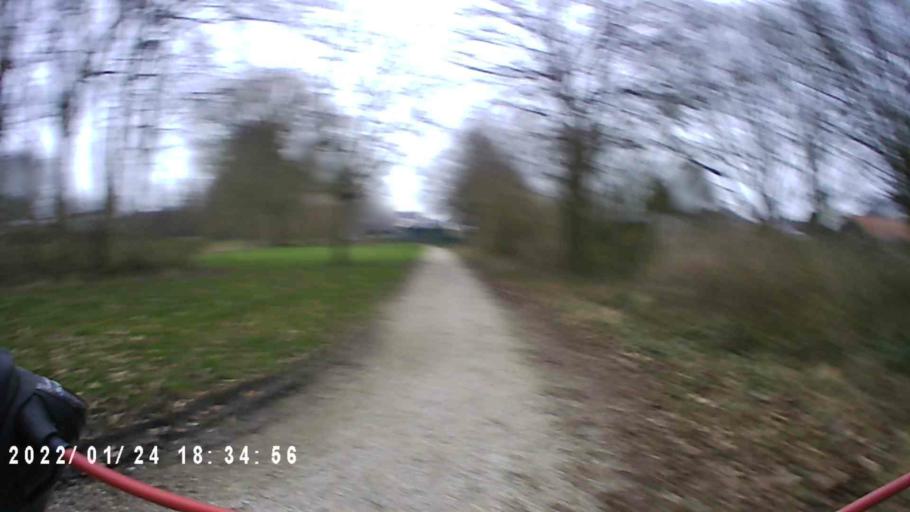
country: NL
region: Groningen
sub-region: Gemeente De Marne
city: Ulrum
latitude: 53.3555
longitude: 6.3366
